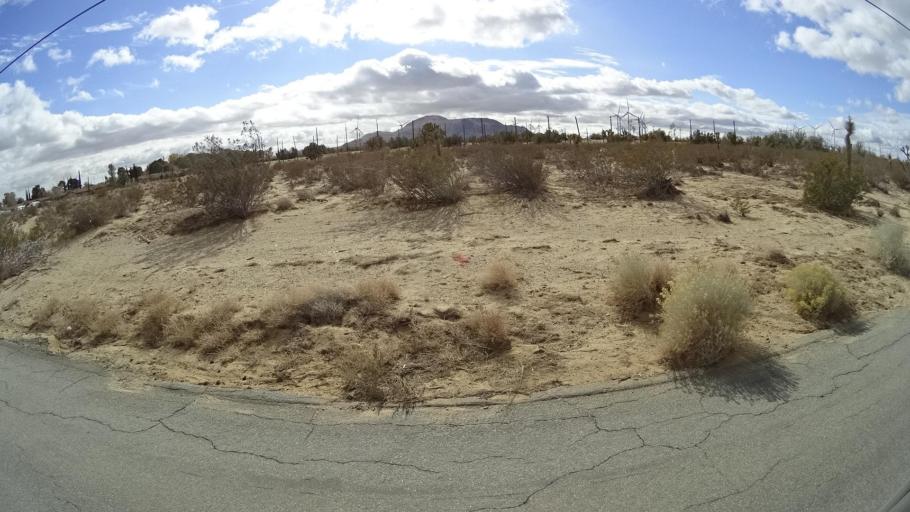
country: US
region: California
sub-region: Kern County
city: Mojave
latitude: 35.0315
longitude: -118.1911
